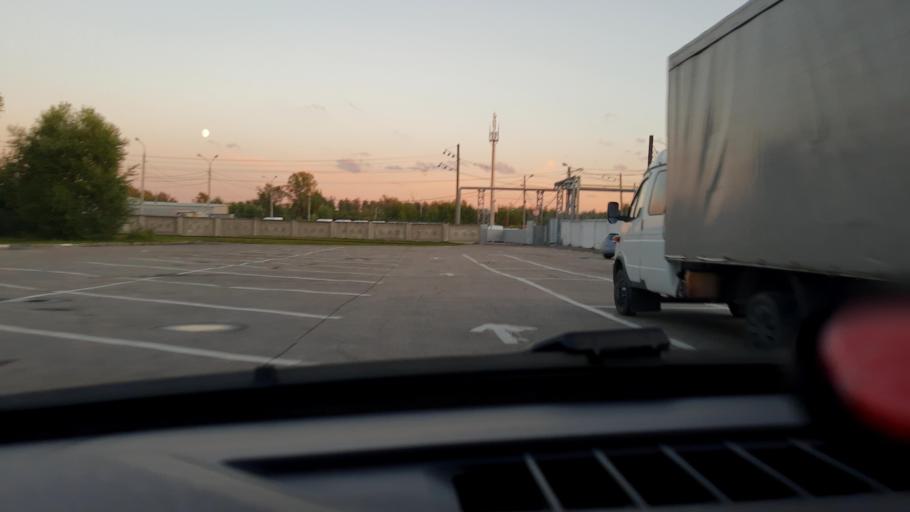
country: RU
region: Nizjnij Novgorod
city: Gorbatovka
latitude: 56.3118
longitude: 43.8478
